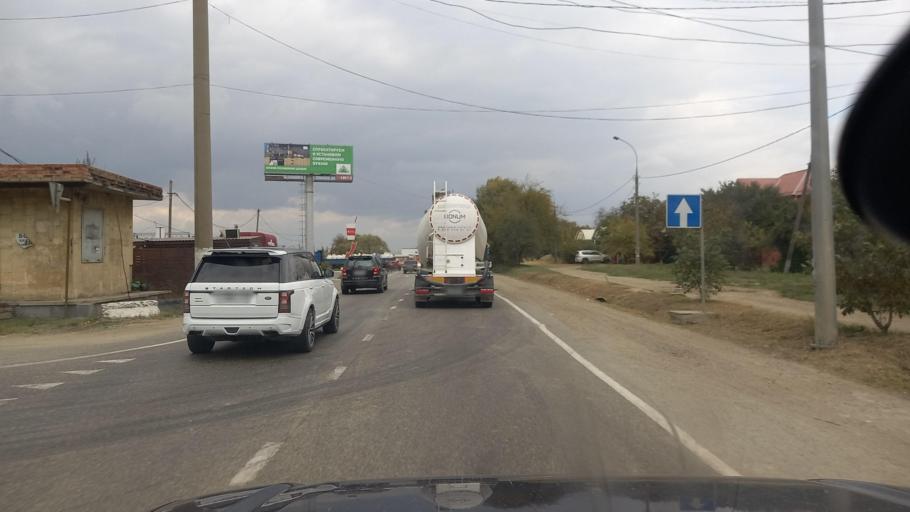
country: RU
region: Adygeya
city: Enem
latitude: 44.9328
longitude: 38.9120
